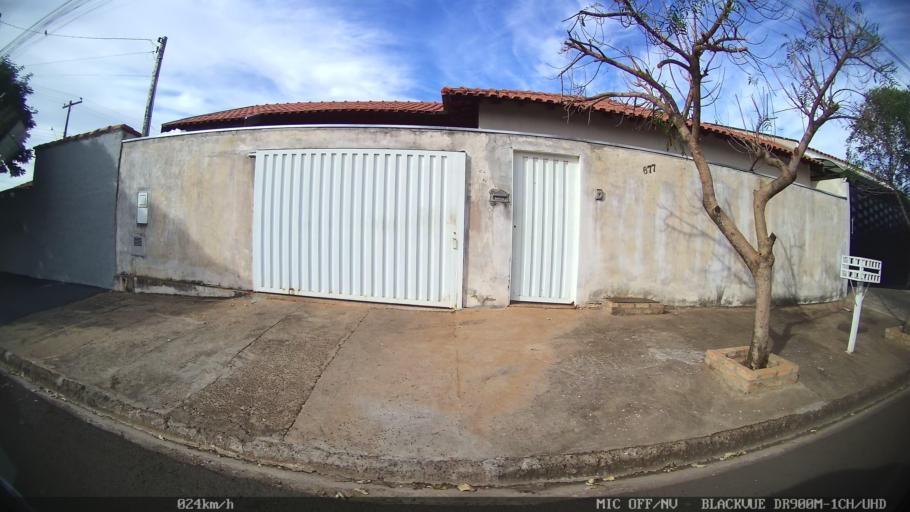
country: BR
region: Sao Paulo
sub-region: Catanduva
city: Catanduva
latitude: -21.1252
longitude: -48.9983
